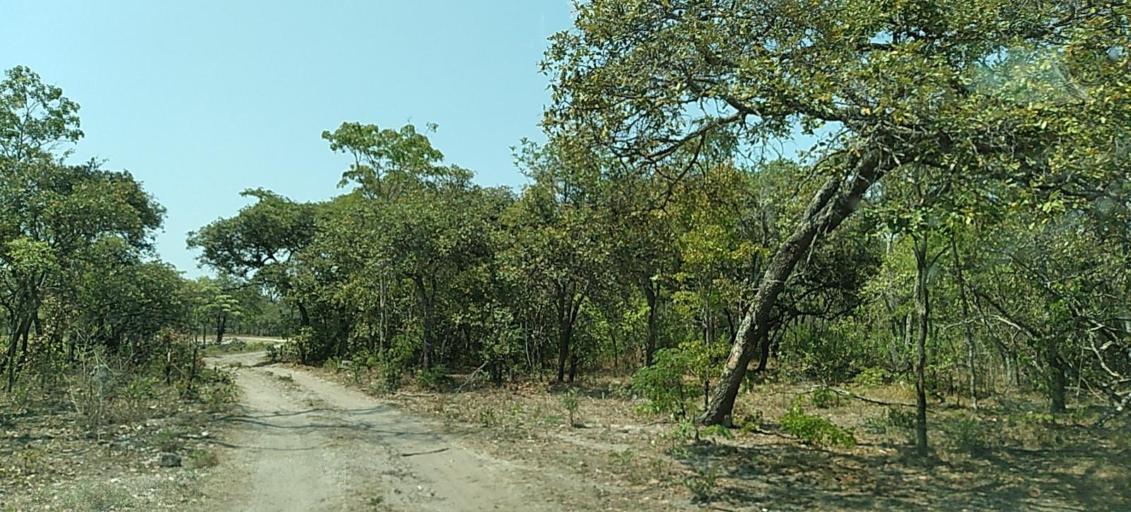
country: ZM
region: Copperbelt
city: Mpongwe
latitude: -13.8463
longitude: 28.0559
